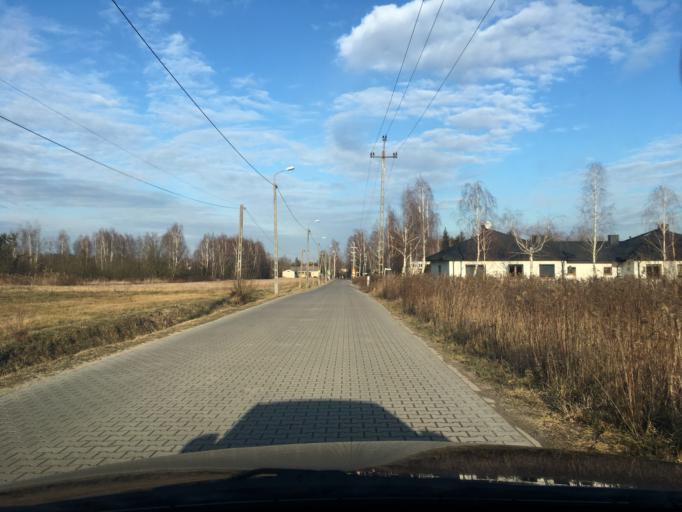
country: PL
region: Masovian Voivodeship
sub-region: Powiat piaseczynski
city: Lesznowola
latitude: 52.0321
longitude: 20.9386
